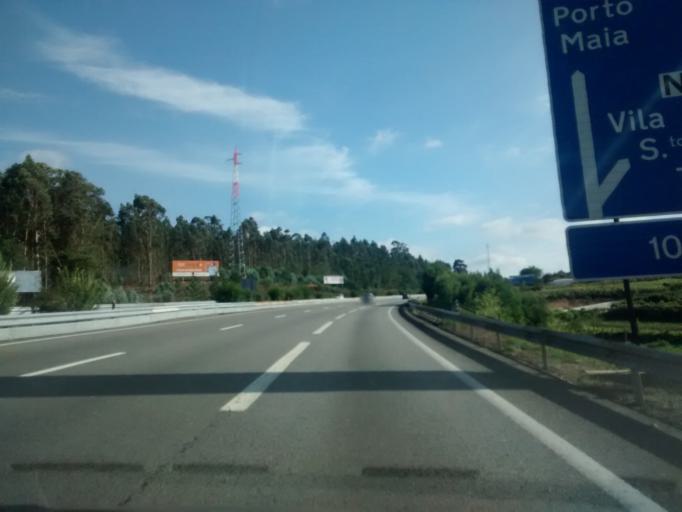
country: PT
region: Porto
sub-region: Santo Tirso
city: Santo Tirso
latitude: 41.3461
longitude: -8.5058
